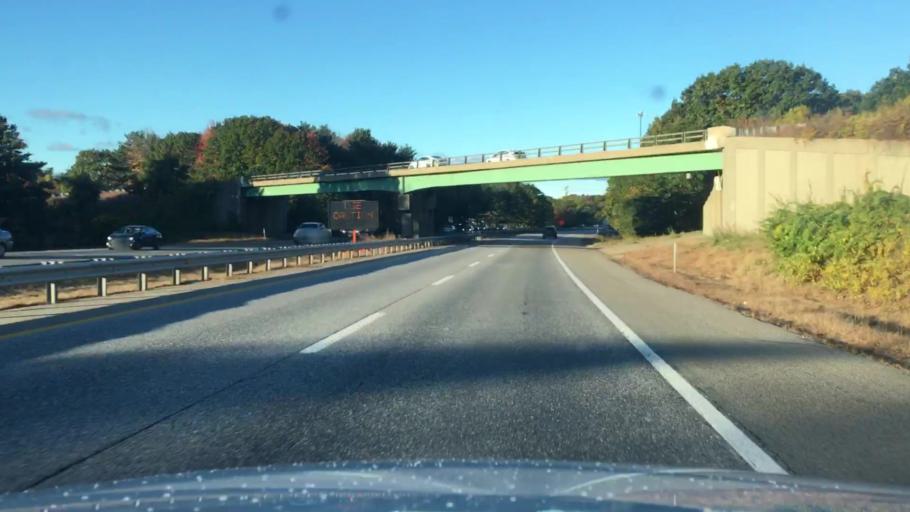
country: US
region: Maine
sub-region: Cumberland County
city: South Portland Gardens
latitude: 43.6293
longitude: -70.3176
